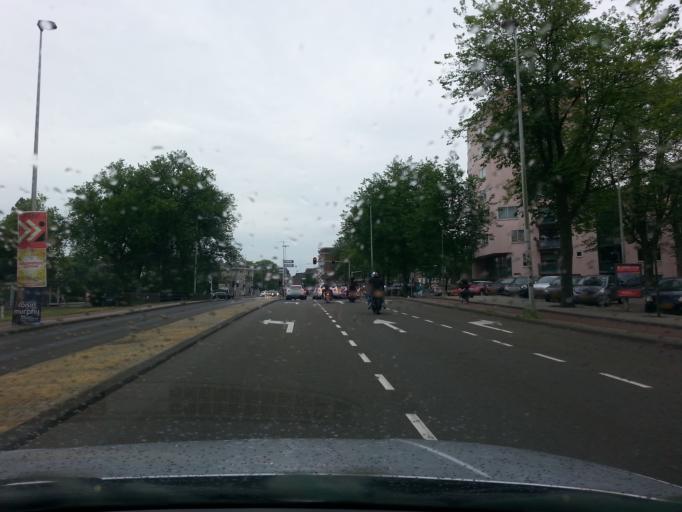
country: NL
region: North Holland
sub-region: Gemeente Amsterdam
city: Amsterdam
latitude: 52.3854
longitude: 4.8799
